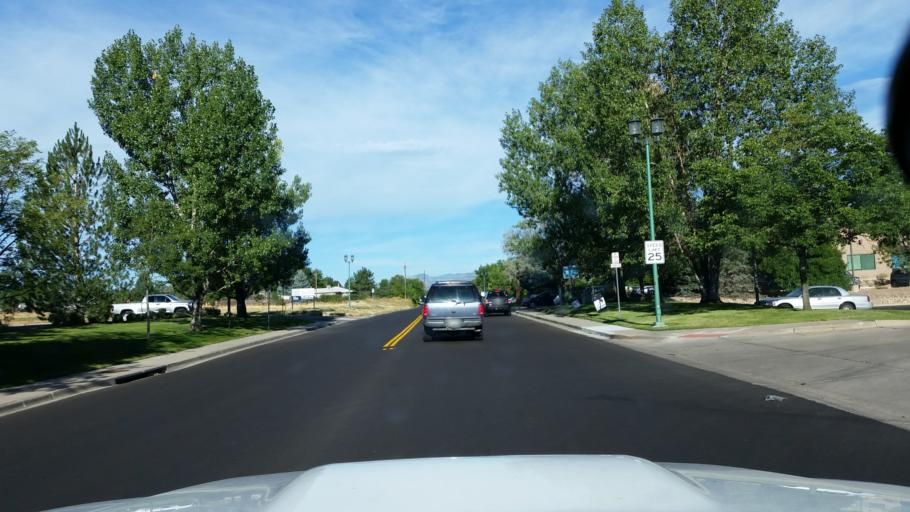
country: US
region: Colorado
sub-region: Broomfield County
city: Broomfield
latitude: 39.8835
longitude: -105.0771
